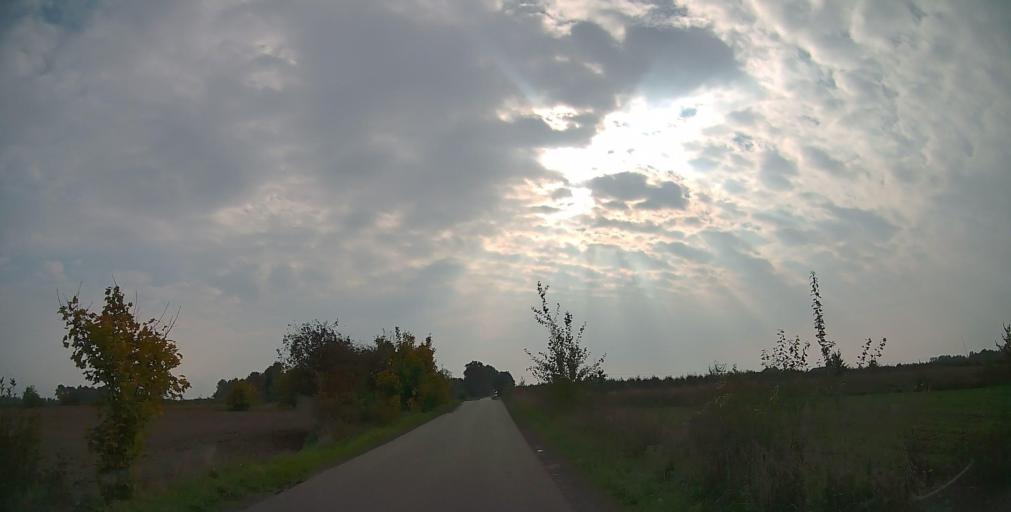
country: PL
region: Masovian Voivodeship
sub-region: Powiat grojecki
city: Mogielnica
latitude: 51.6582
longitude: 20.7151
